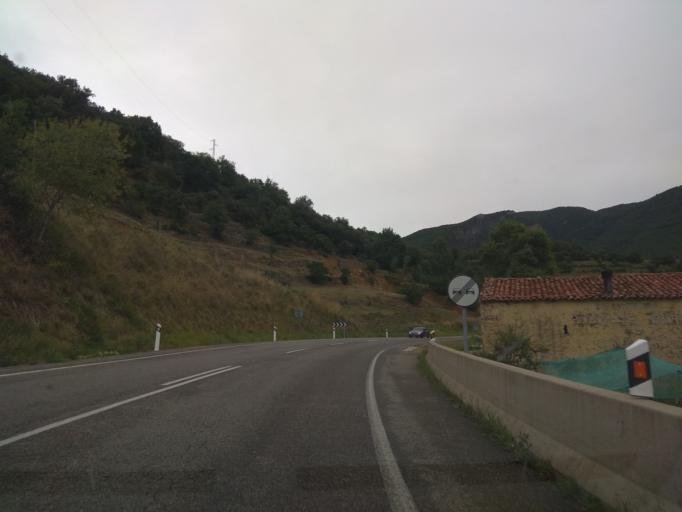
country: ES
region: Catalonia
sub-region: Provincia de Lleida
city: el Pont de Bar
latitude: 42.3621
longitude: 1.5733
